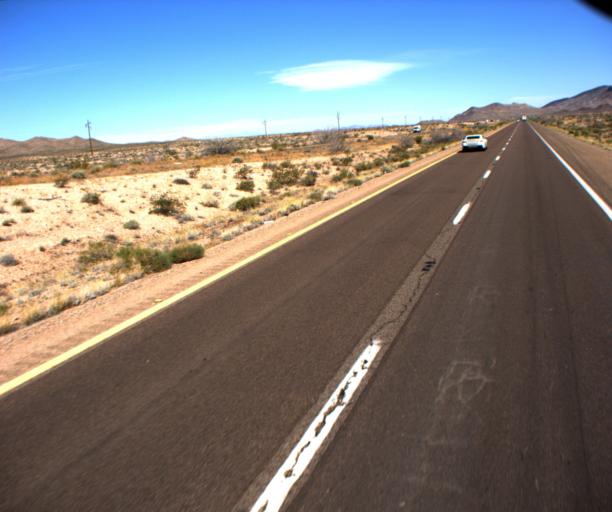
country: US
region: Nevada
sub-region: Clark County
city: Boulder City
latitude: 35.8137
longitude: -114.5467
